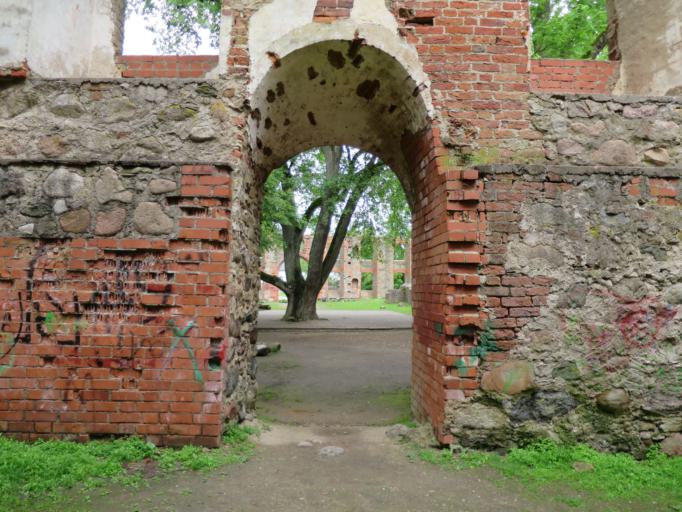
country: LV
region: Grobina
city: Grobina
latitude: 56.5343
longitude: 21.1626
